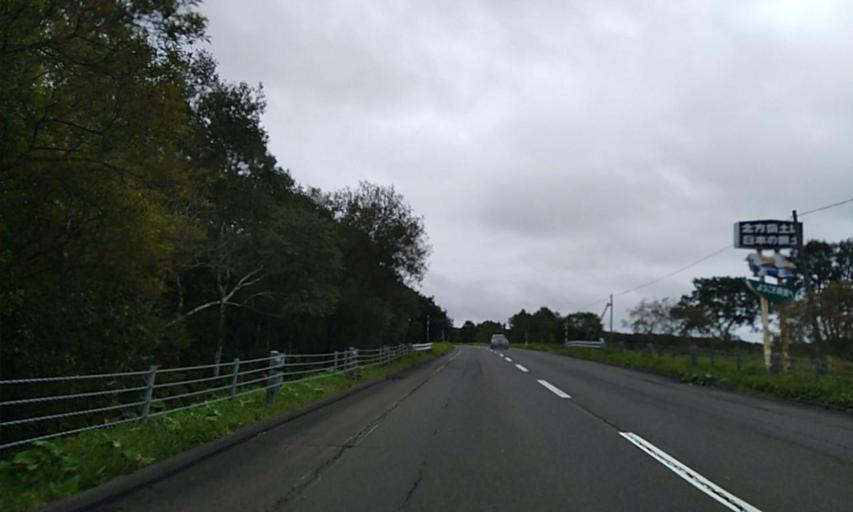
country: JP
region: Hokkaido
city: Nemuro
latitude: 43.2653
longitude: 145.2403
